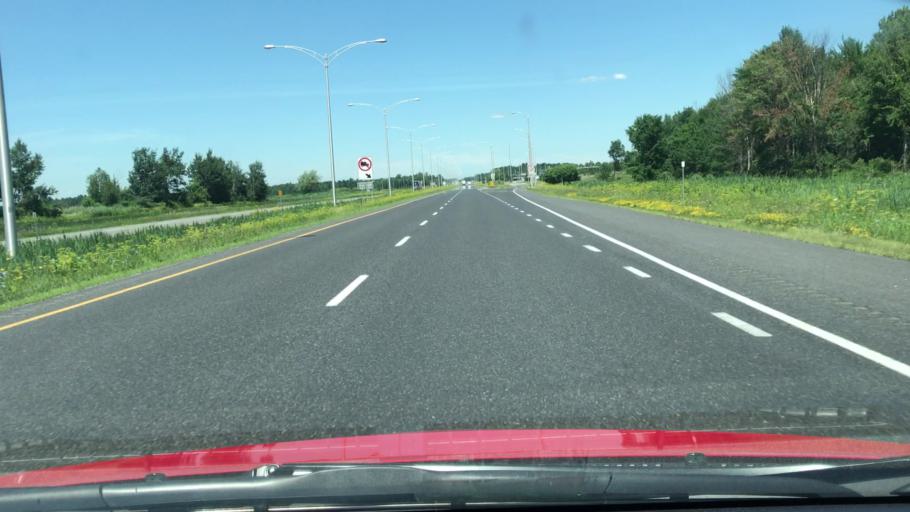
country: US
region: New York
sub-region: Clinton County
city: Champlain
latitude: 45.0308
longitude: -73.4533
